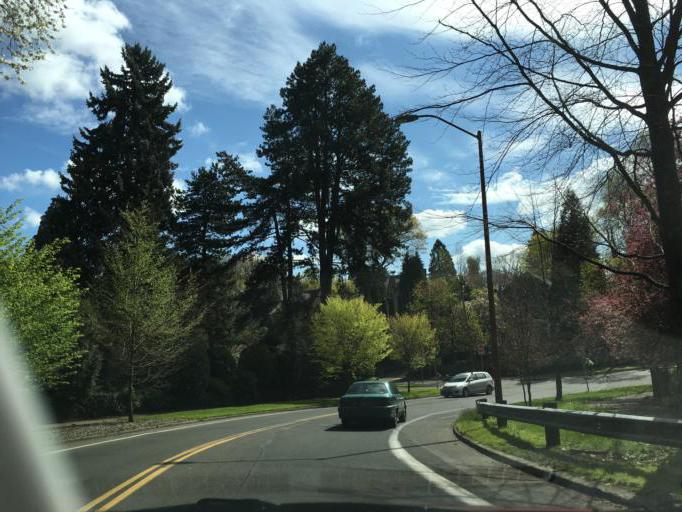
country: US
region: Oregon
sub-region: Clackamas County
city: Milwaukie
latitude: 45.4781
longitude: -122.6343
